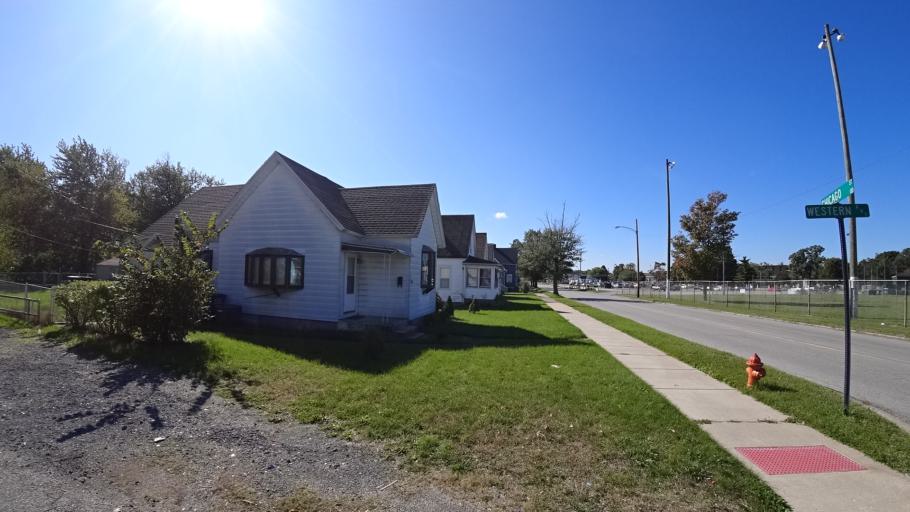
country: US
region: Indiana
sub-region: LaPorte County
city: Michigan City
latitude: 41.7051
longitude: -86.9120
